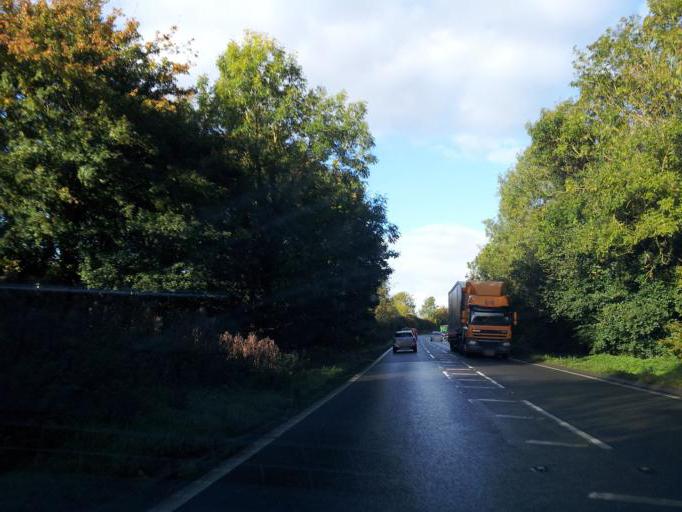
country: GB
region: England
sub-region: Norfolk
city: Hethersett
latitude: 52.6571
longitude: 1.1275
